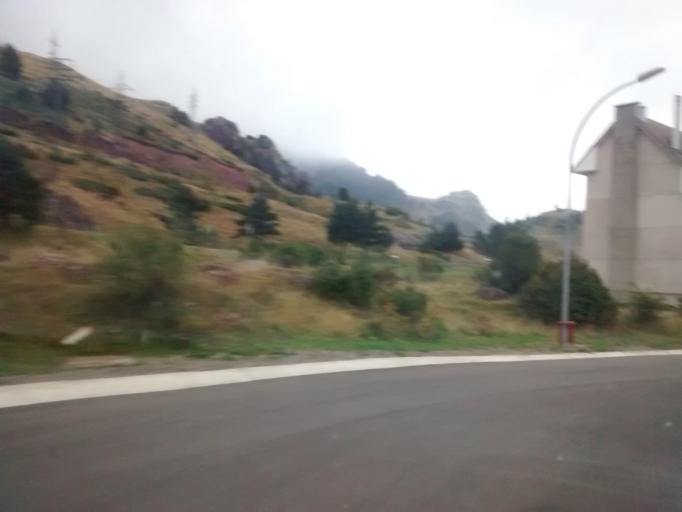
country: ES
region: Aragon
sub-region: Provincia de Huesca
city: Canfranc
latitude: 42.7870
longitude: -0.5252
